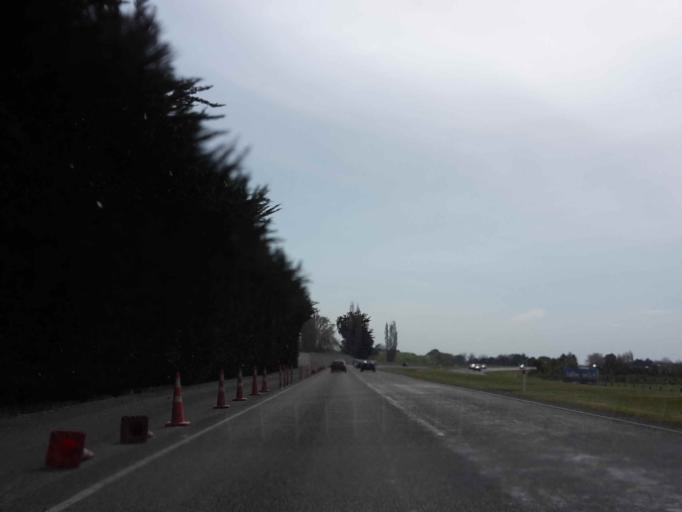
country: NZ
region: Canterbury
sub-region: Waimakariri District
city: Kaiapoi
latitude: -43.4351
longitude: 172.6388
